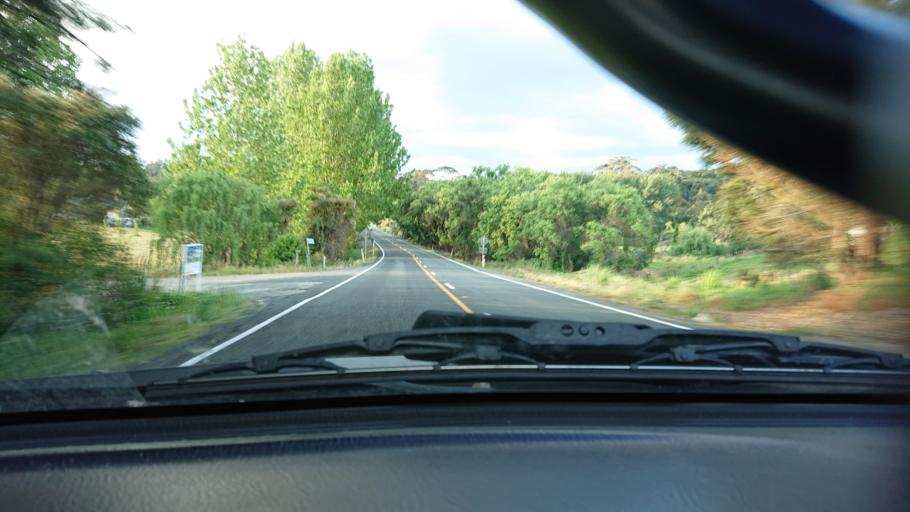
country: NZ
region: Auckland
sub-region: Auckland
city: Parakai
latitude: -36.5345
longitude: 174.4567
